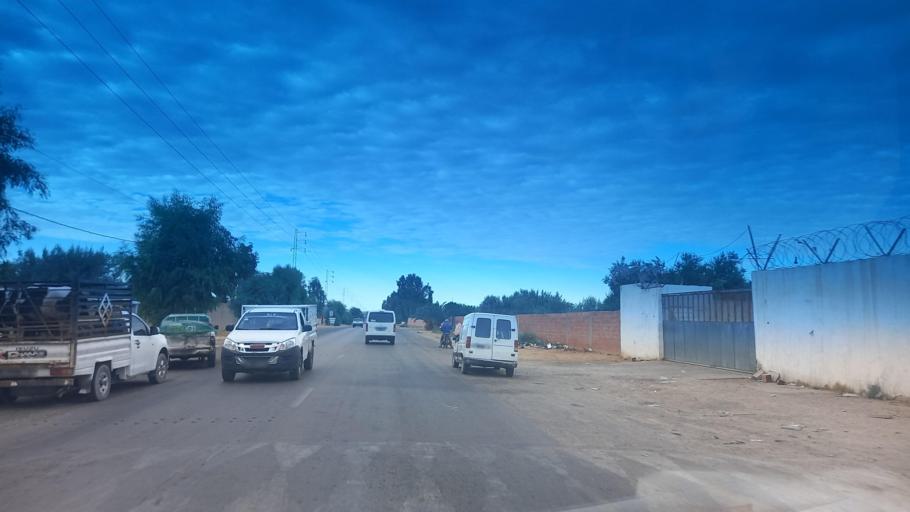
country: TN
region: Al Qasrayn
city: Sbiba
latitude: 35.2691
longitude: 9.0931
